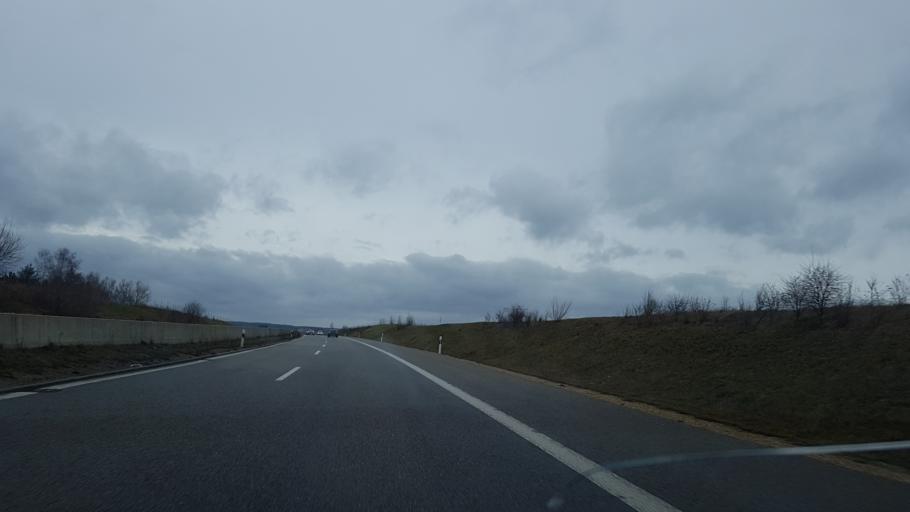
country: DE
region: Bavaria
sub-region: Upper Palatinate
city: Schierling
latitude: 48.8258
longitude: 12.1296
